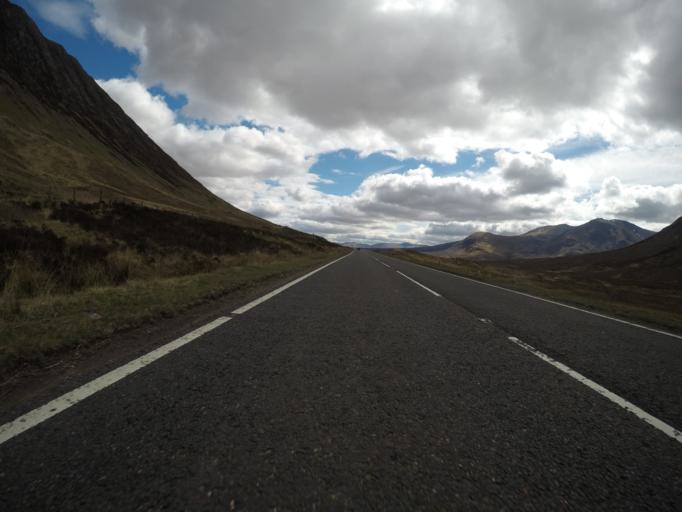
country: GB
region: Scotland
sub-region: Highland
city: Spean Bridge
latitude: 56.6621
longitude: -4.8937
